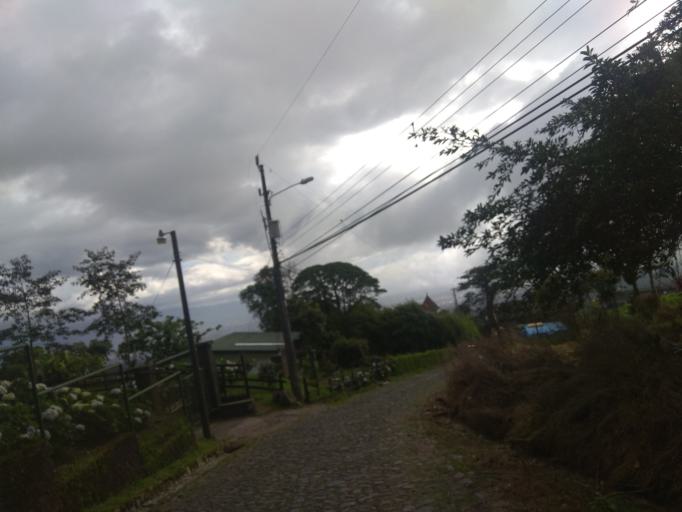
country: CR
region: San Jose
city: Ipis
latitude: 9.9864
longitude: -83.9579
